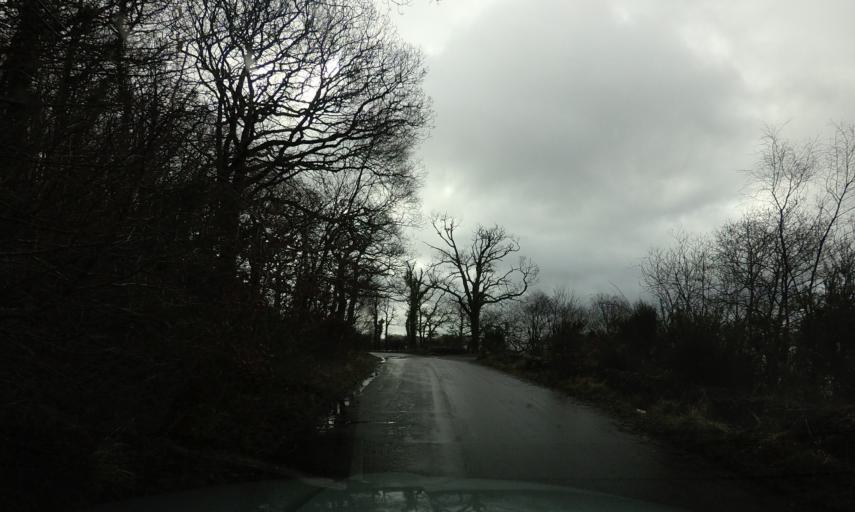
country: GB
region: Scotland
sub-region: West Dunbartonshire
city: Balloch
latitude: 56.1149
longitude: -4.5857
